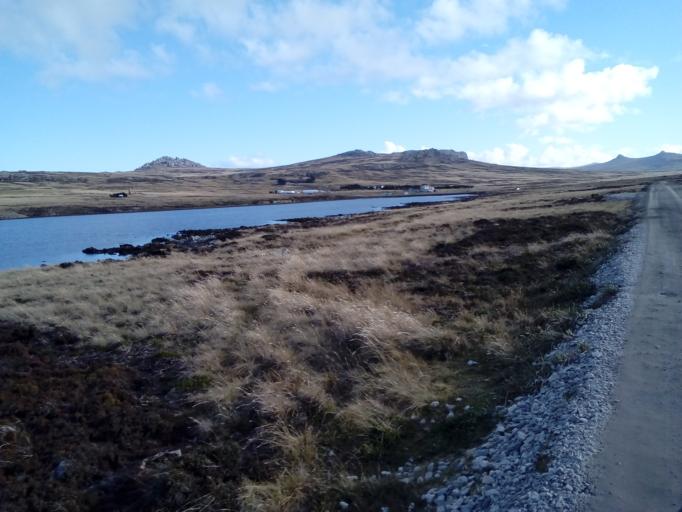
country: FK
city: Stanley
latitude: -51.6843
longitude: -57.9126
